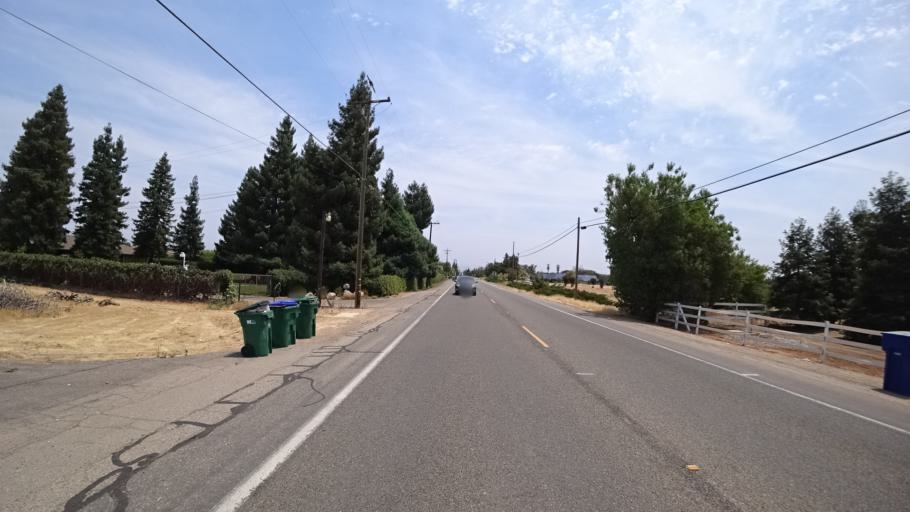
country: US
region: California
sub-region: Fresno County
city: Sunnyside
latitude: 36.7504
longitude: -119.6674
